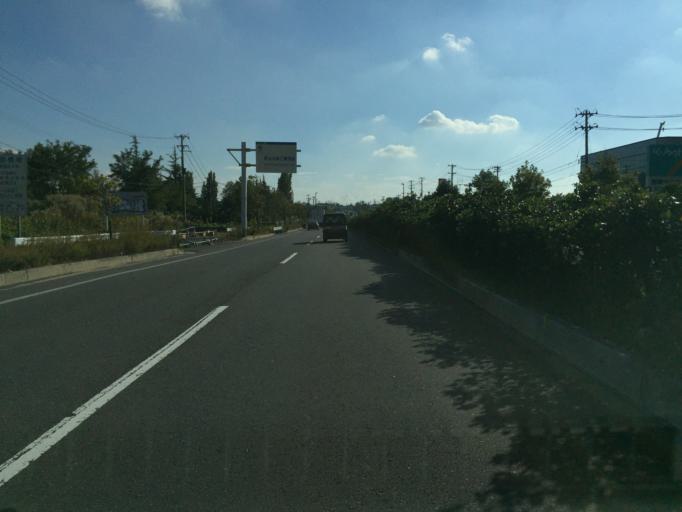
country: JP
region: Fukushima
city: Motomiya
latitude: 37.4757
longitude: 140.3786
